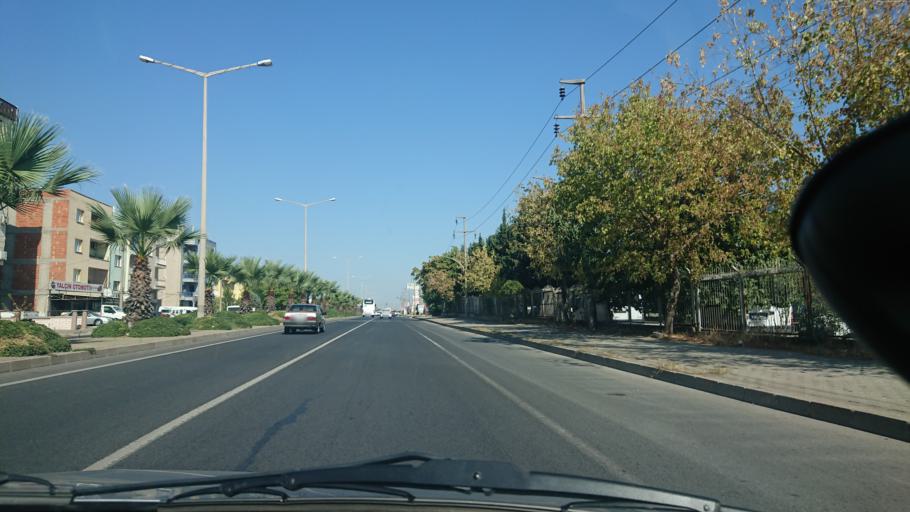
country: TR
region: Manisa
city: Turgutlu
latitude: 38.4939
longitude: 27.7174
